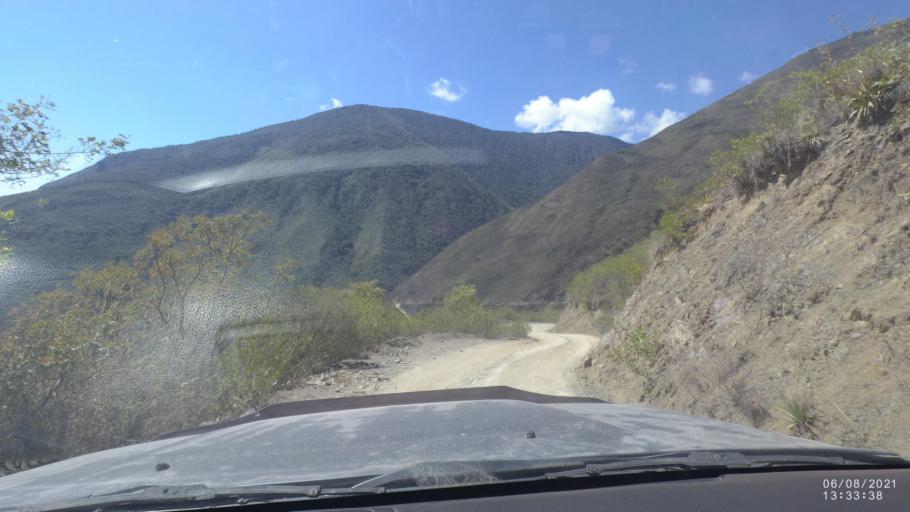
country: BO
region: La Paz
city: Quime
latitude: -16.6967
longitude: -66.7259
